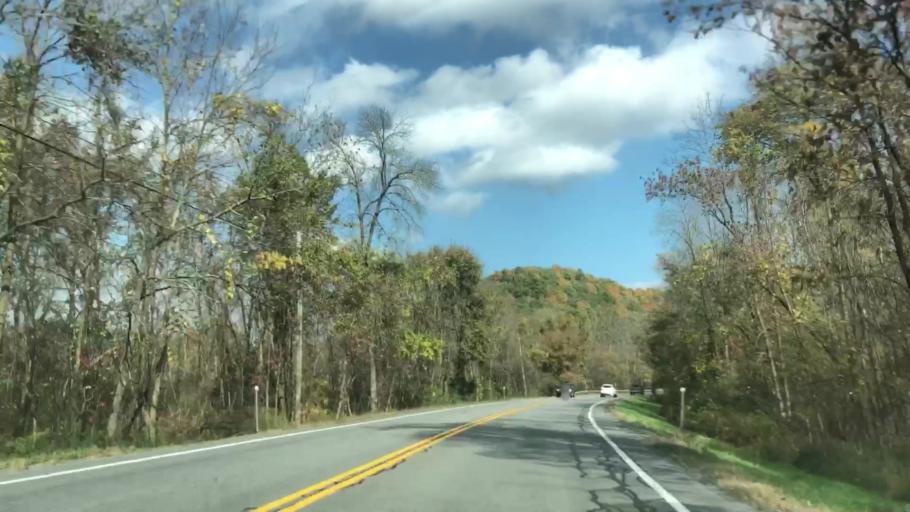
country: US
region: New York
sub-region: Warren County
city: Queensbury
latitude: 43.4225
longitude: -73.4845
